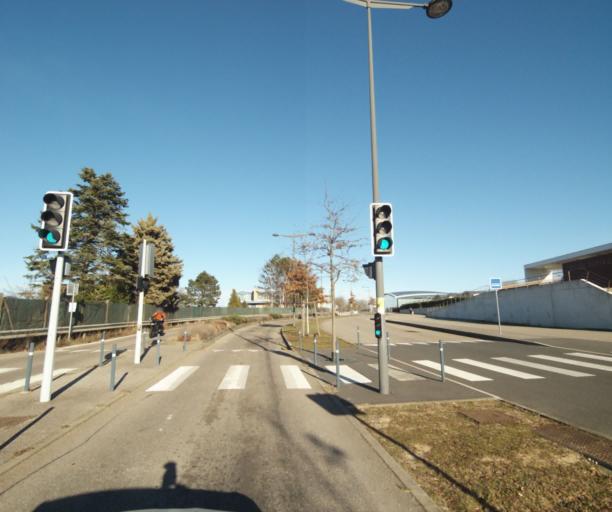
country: FR
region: Lorraine
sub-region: Departement de Meurthe-et-Moselle
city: Heillecourt
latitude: 48.6574
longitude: 6.2081
